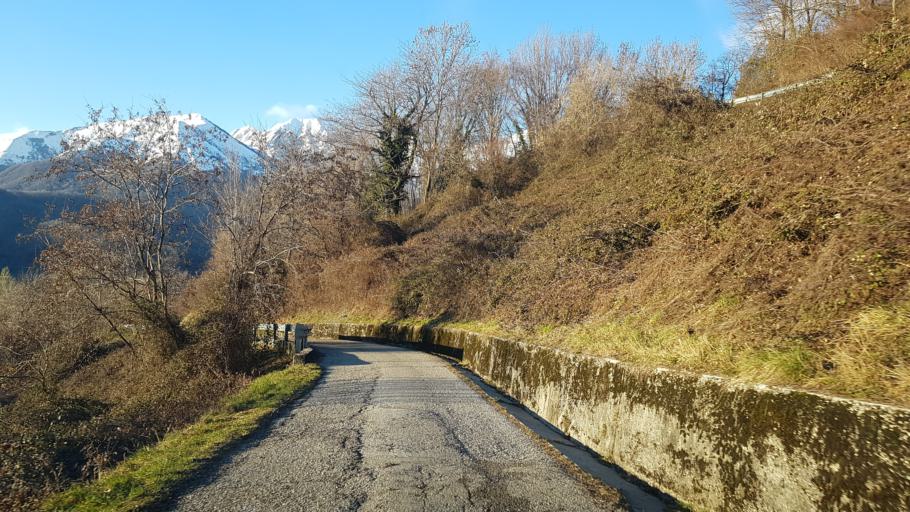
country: IT
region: Friuli Venezia Giulia
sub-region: Provincia di Udine
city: Tarcento
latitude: 46.2467
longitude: 13.2255
